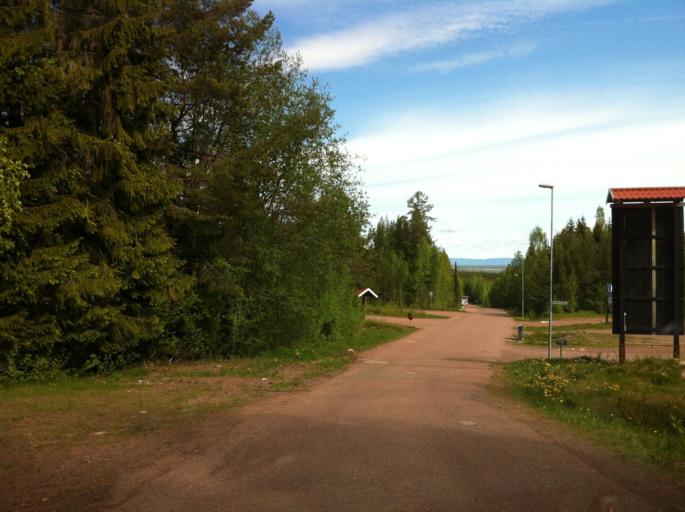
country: SE
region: Dalarna
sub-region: Mora Kommun
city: Mora
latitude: 60.8777
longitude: 14.5184
